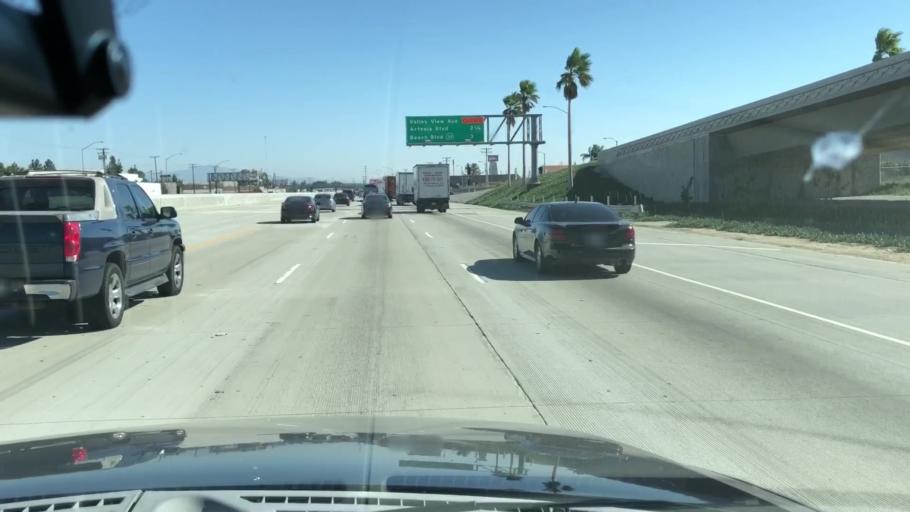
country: US
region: California
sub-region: Los Angeles County
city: Norwalk
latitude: 33.8930
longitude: -118.0461
